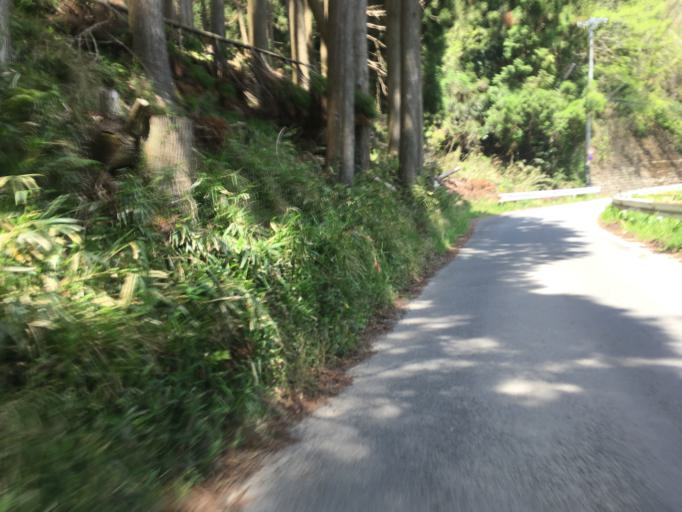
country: JP
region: Kyoto
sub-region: Kyoto-shi
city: Kamigyo-ku
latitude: 35.1088
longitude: 135.7361
